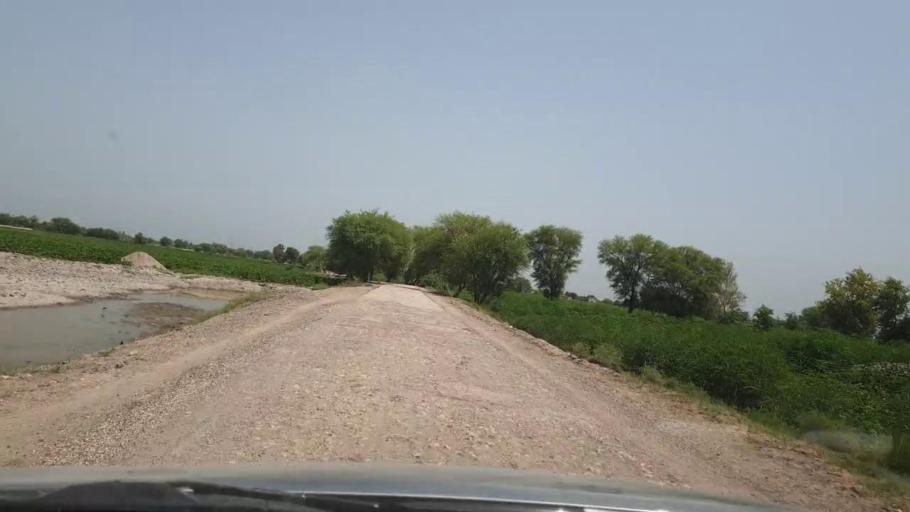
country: PK
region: Sindh
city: Pano Aqil
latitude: 27.8253
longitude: 69.2151
